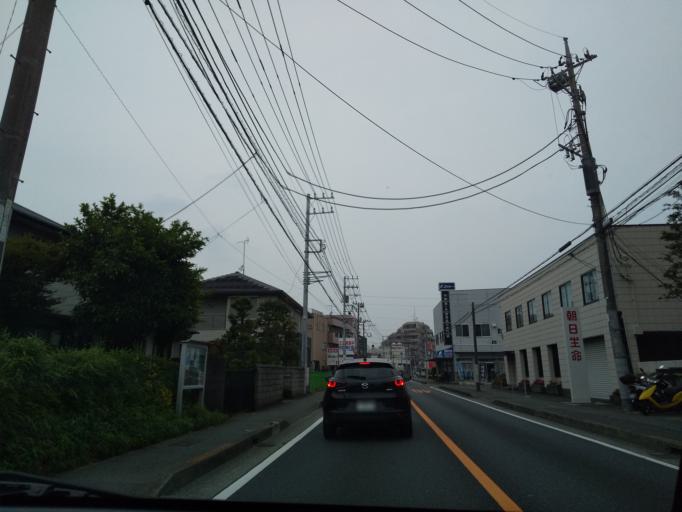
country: JP
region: Kanagawa
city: Zama
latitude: 35.5025
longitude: 139.4100
